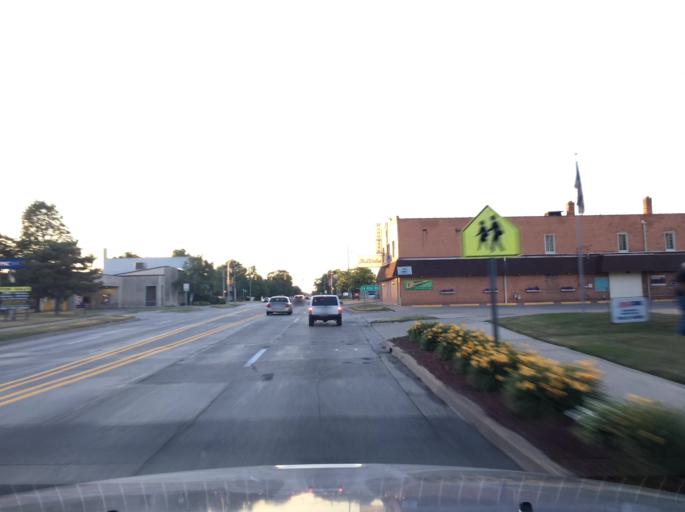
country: US
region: Michigan
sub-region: Macomb County
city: Fraser
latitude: 42.5376
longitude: -82.9521
